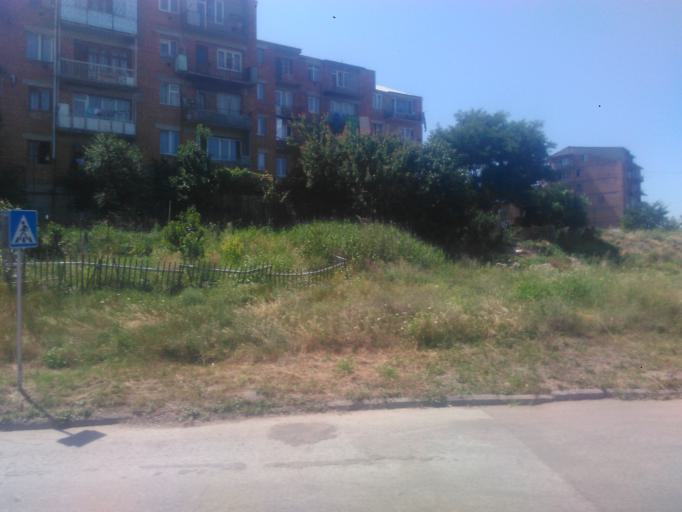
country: GE
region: T'bilisi
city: Tbilisi
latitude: 41.7061
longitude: 44.8863
